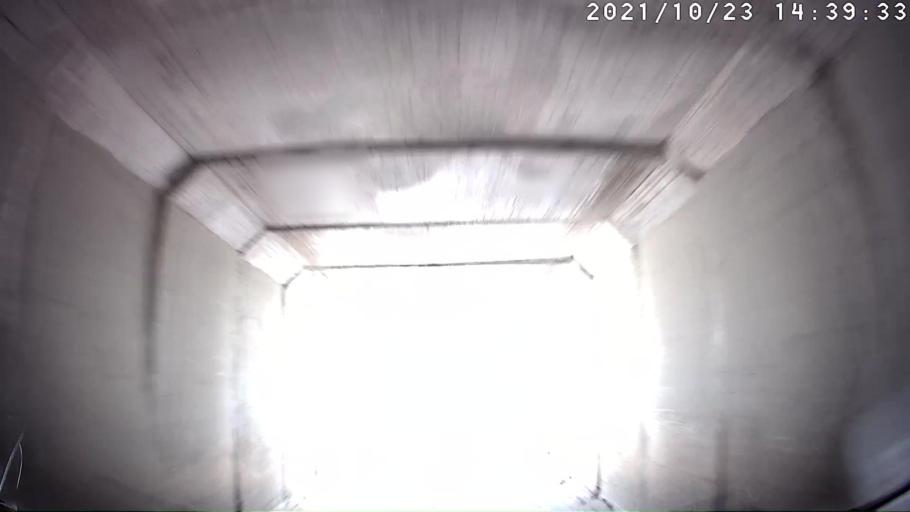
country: RU
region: Volgograd
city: Krasnoslobodsk
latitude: 48.4854
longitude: 44.5460
